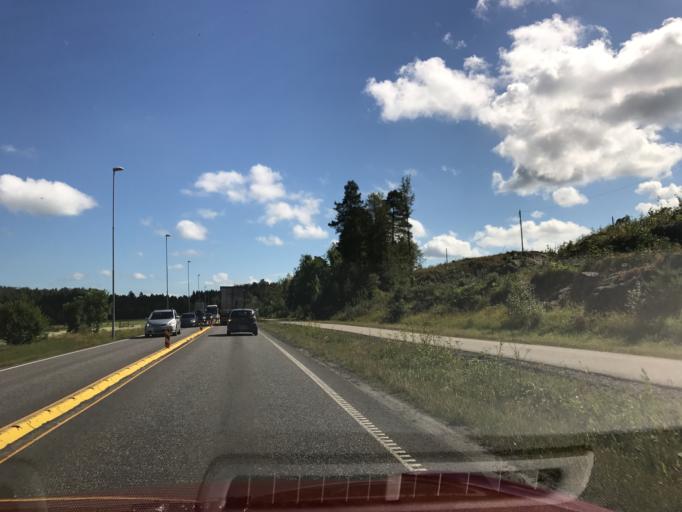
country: NO
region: Telemark
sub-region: Bamble
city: Langesund
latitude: 59.0321
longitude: 9.6776
